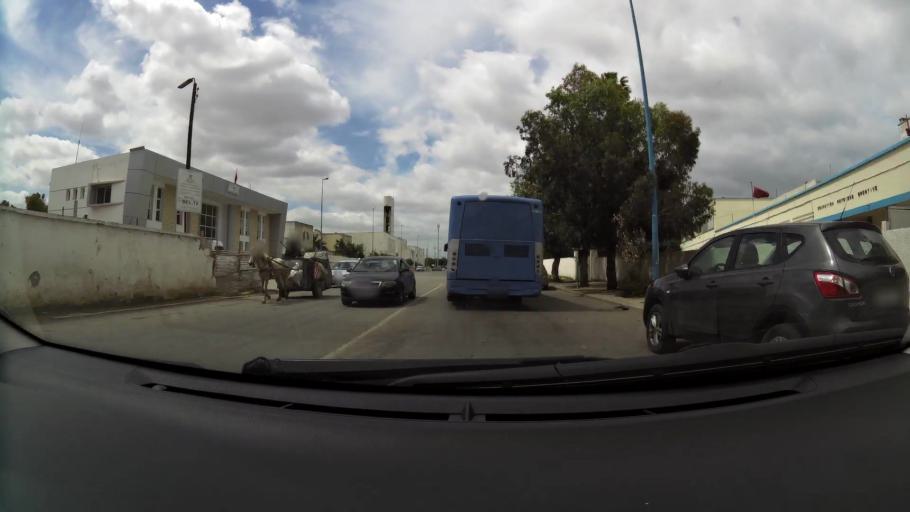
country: MA
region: Grand Casablanca
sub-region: Casablanca
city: Casablanca
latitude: 33.6066
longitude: -7.5498
